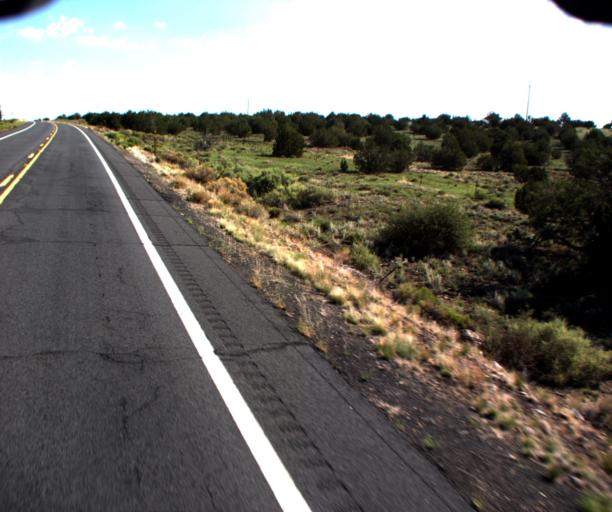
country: US
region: Arizona
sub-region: Coconino County
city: Williams
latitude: 35.4862
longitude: -112.1752
